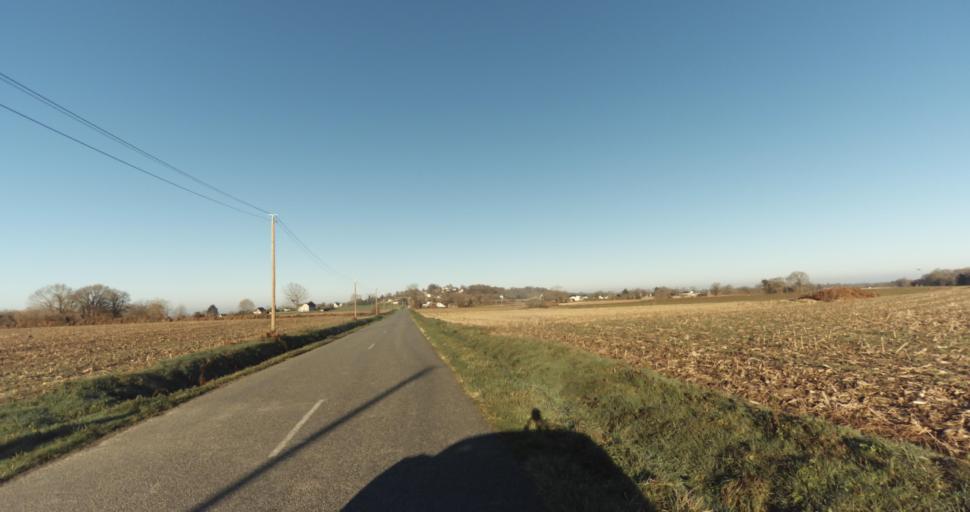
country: FR
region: Aquitaine
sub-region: Departement des Pyrenees-Atlantiques
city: Morlaas
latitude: 43.3188
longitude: -0.2447
